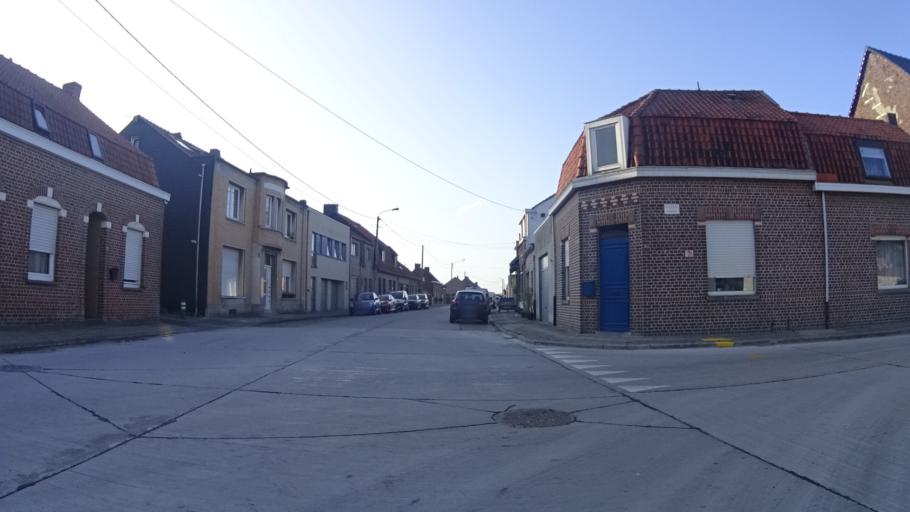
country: FR
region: Nord-Pas-de-Calais
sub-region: Departement du Nord
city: Comines
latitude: 50.7961
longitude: 2.9610
